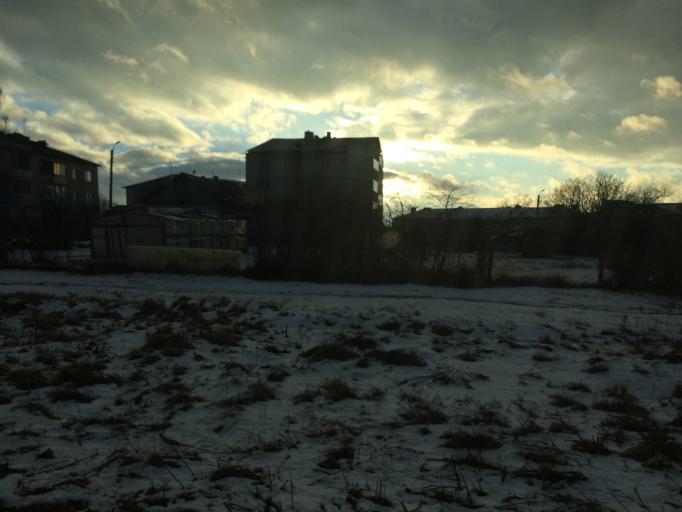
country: RU
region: Tula
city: Cherepet'
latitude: 54.1079
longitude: 36.3288
